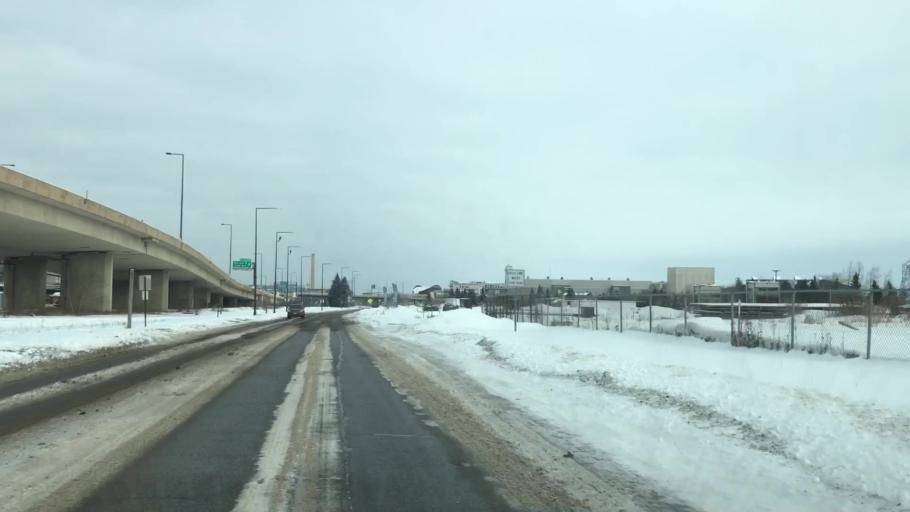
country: US
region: Minnesota
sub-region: Saint Louis County
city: Duluth
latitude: 46.7773
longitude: -92.1068
